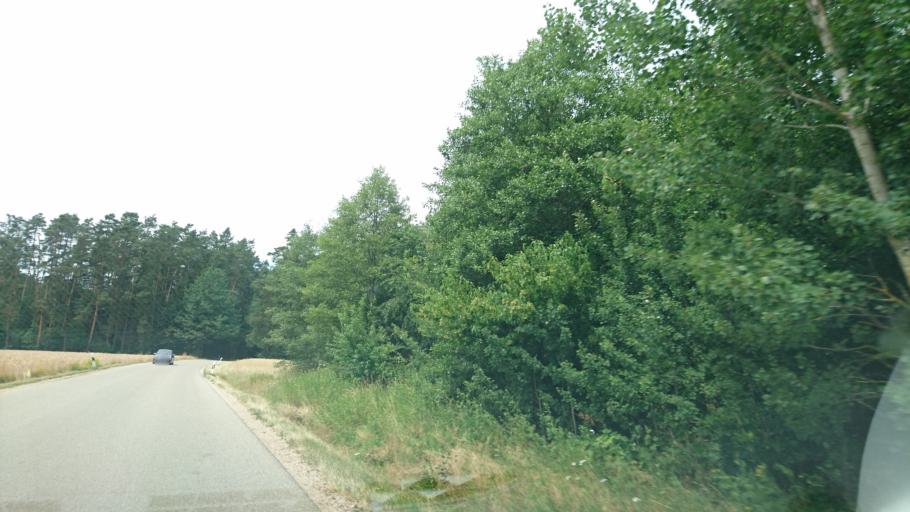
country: DE
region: Bavaria
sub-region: Regierungsbezirk Mittelfranken
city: Roth
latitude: 49.1975
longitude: 11.0972
